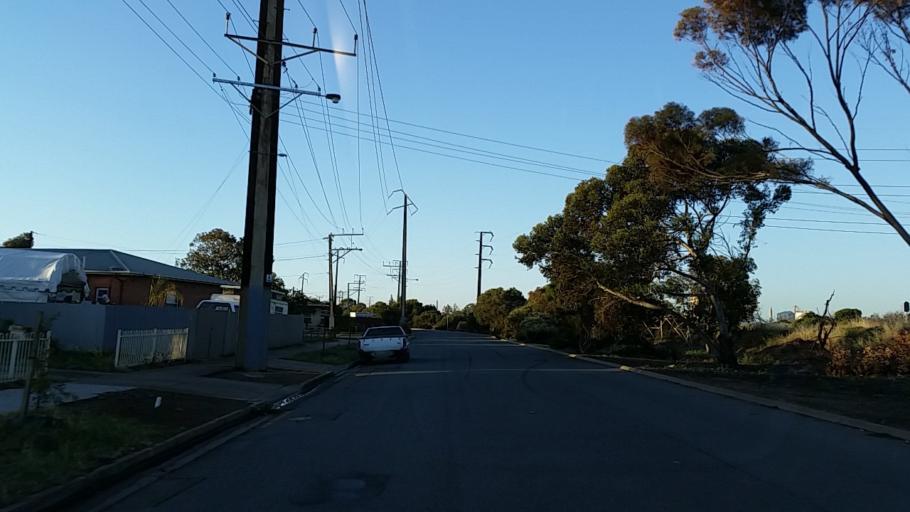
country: AU
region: South Australia
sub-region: Port Adelaide Enfield
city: Birkenhead
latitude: -34.8064
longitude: 138.5064
